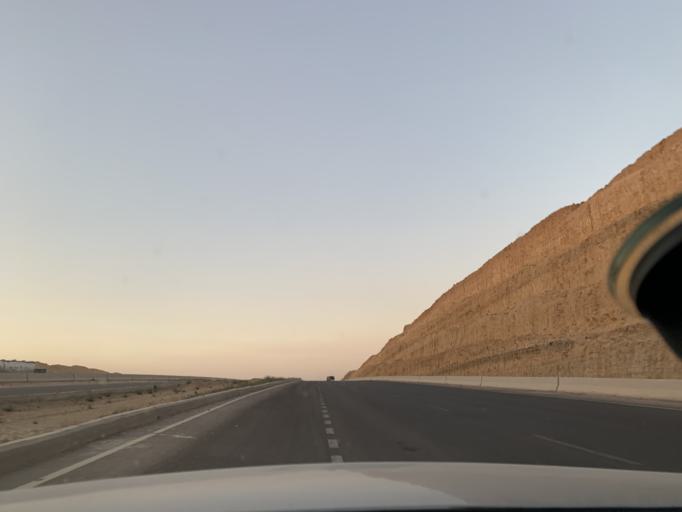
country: EG
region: Muhafazat al Qahirah
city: Halwan
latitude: 29.9502
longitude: 31.5383
